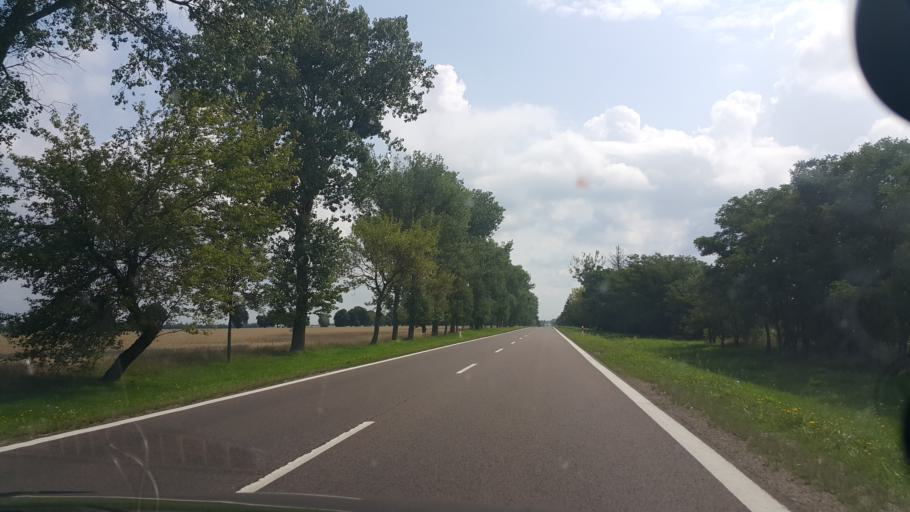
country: PL
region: Lublin Voivodeship
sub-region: Powiat wlodawski
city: Wlodawa
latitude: 51.5445
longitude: 23.5060
